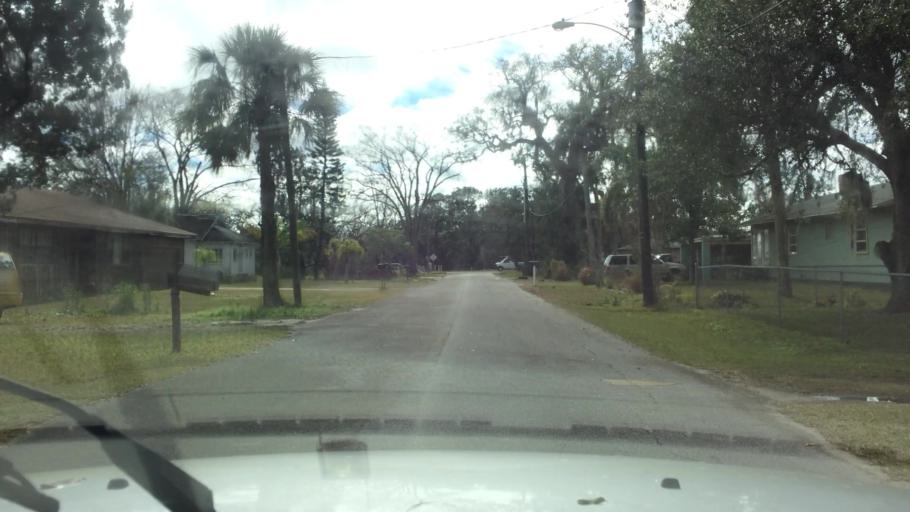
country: US
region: Florida
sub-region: Volusia County
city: Holly Hill
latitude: 29.2319
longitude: -81.0492
